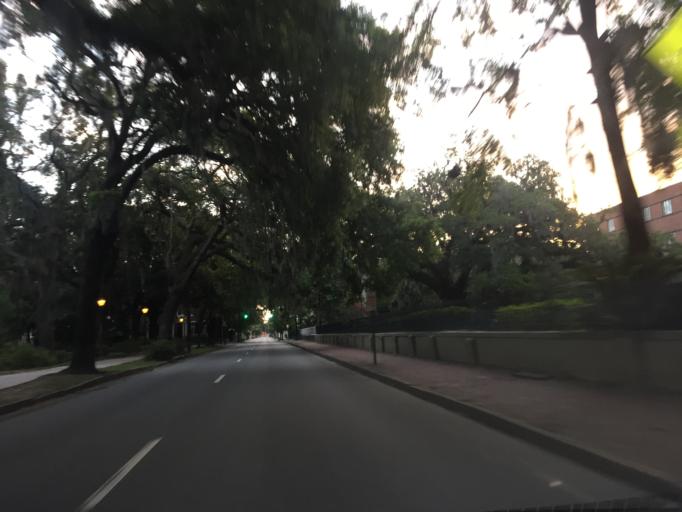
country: US
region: Georgia
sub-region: Chatham County
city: Savannah
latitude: 32.0689
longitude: -81.0945
